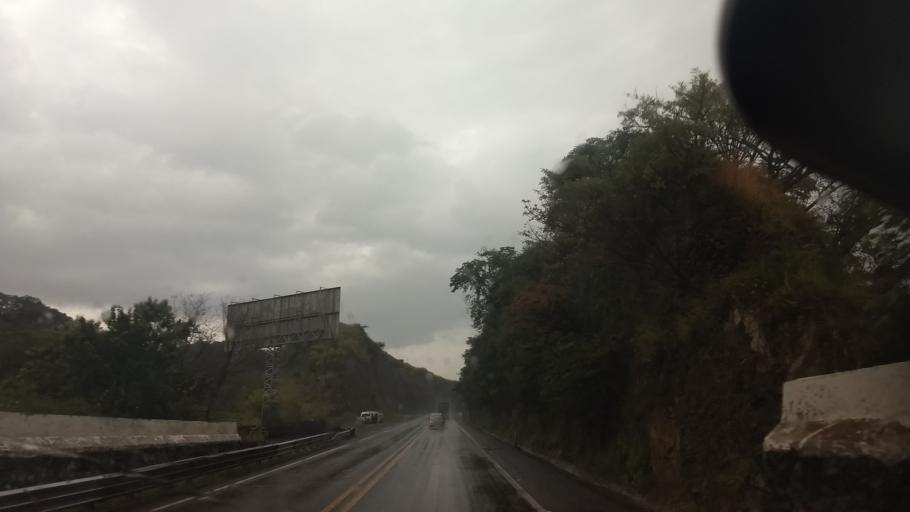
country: MX
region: Jalisco
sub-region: Tonila
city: San Marcos
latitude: 19.4458
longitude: -103.4745
